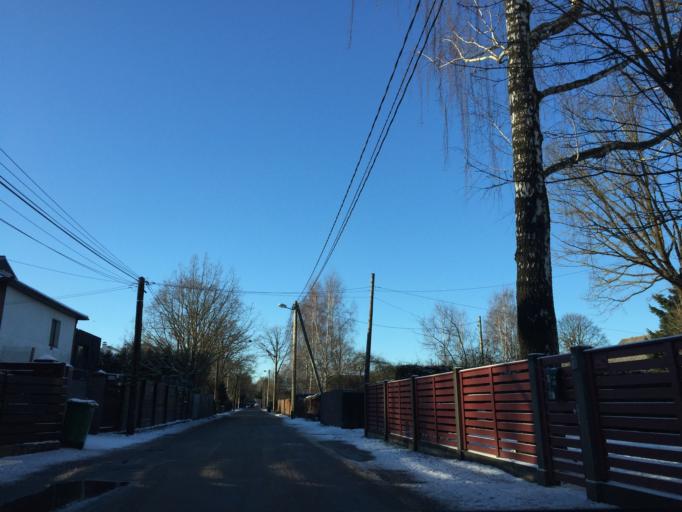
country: LV
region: Marupe
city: Marupe
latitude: 56.9123
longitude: 24.0627
